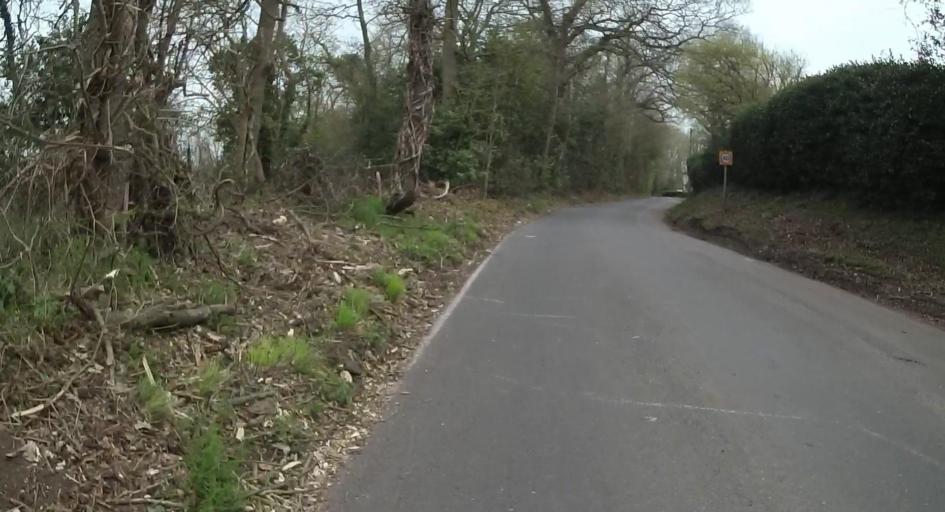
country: GB
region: England
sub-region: West Berkshire
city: Arborfield
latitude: 51.4034
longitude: -0.9137
